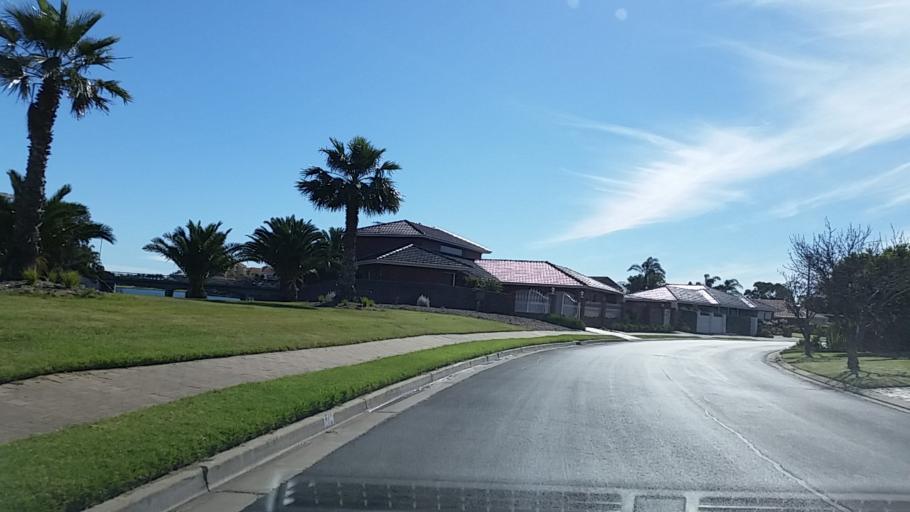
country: AU
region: South Australia
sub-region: Charles Sturt
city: West Lakes Shore
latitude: -34.8751
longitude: 138.4936
